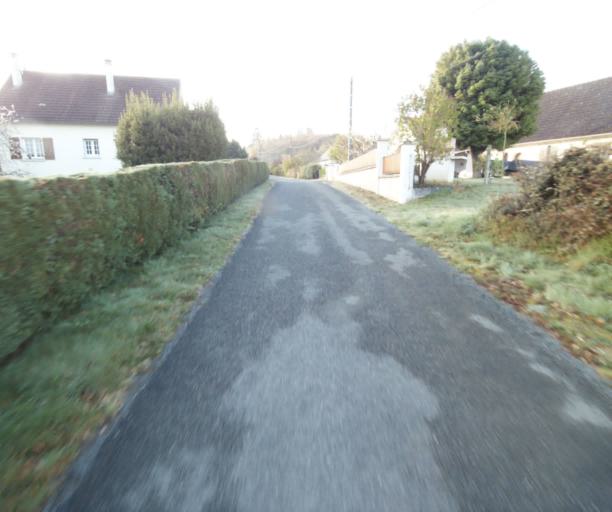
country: FR
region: Limousin
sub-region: Departement de la Correze
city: Naves
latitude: 45.3146
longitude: 1.8210
